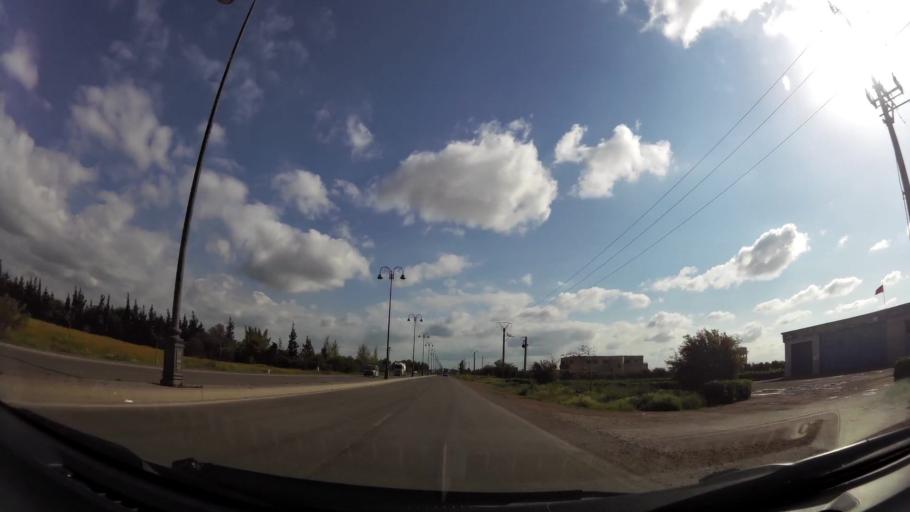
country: MA
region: Chaouia-Ouardigha
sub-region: Settat Province
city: Berrechid
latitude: 33.2939
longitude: -7.5749
